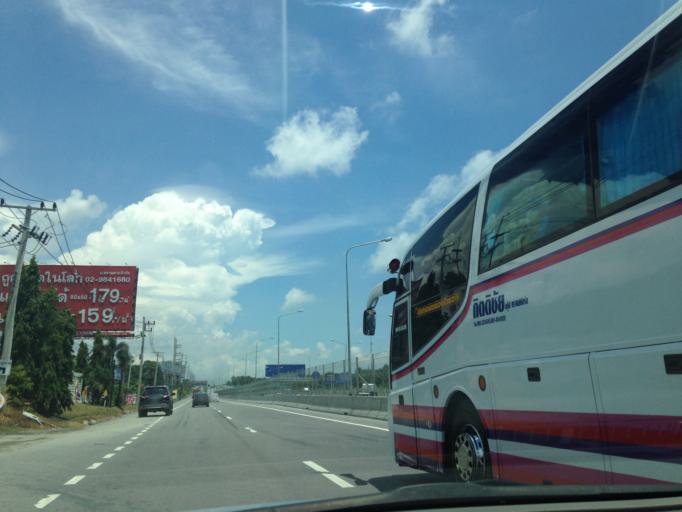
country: TH
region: Chon Buri
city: Chon Buri
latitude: 13.2778
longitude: 100.9909
